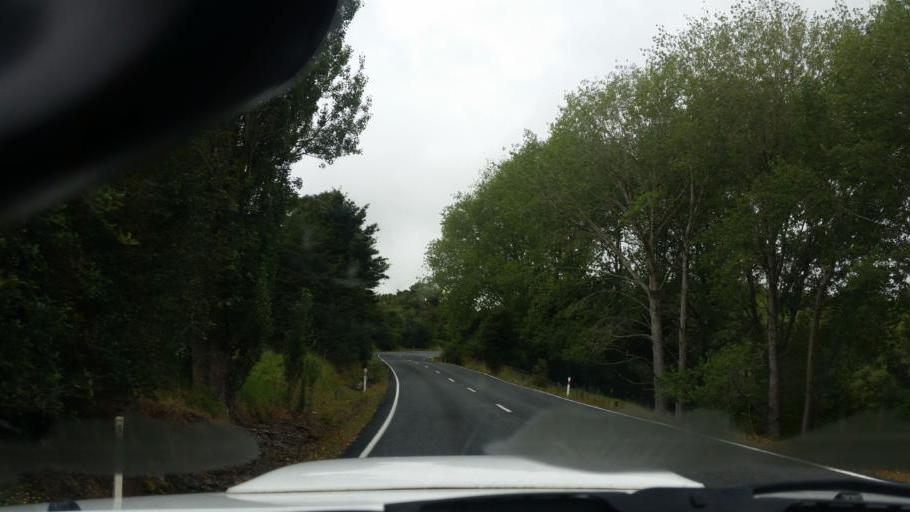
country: NZ
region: Auckland
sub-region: Auckland
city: Wellsford
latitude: -36.1539
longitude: 174.4673
